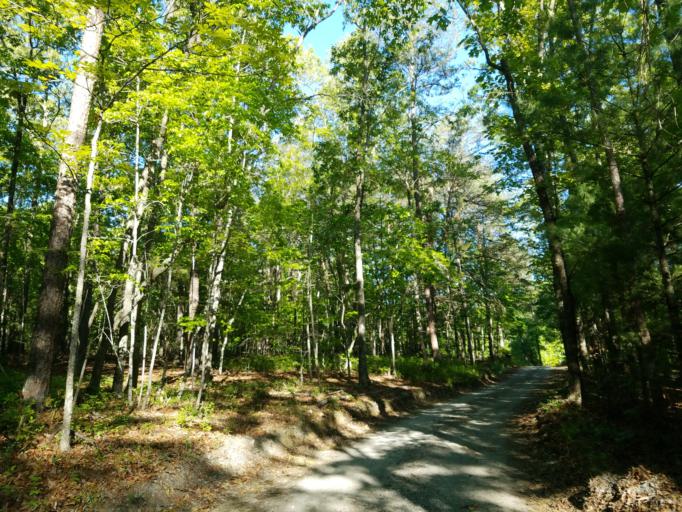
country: US
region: Georgia
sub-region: Fannin County
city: Blue Ridge
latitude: 34.8531
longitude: -84.1972
